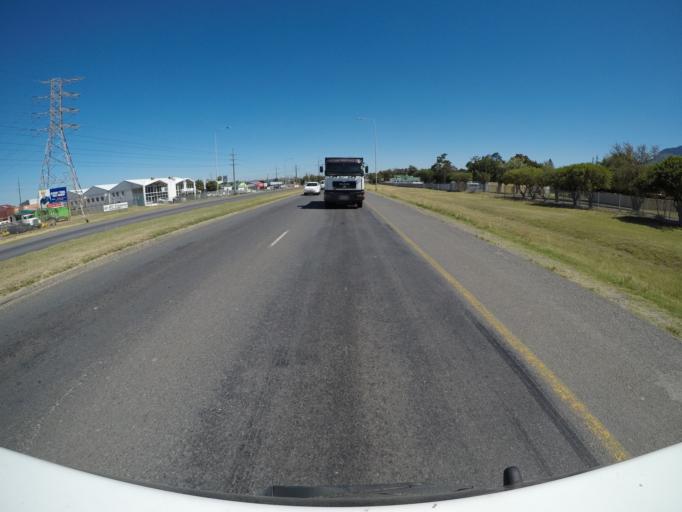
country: ZA
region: Western Cape
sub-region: Cape Winelands District Municipality
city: Stellenbosch
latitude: -34.0930
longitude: 18.8435
